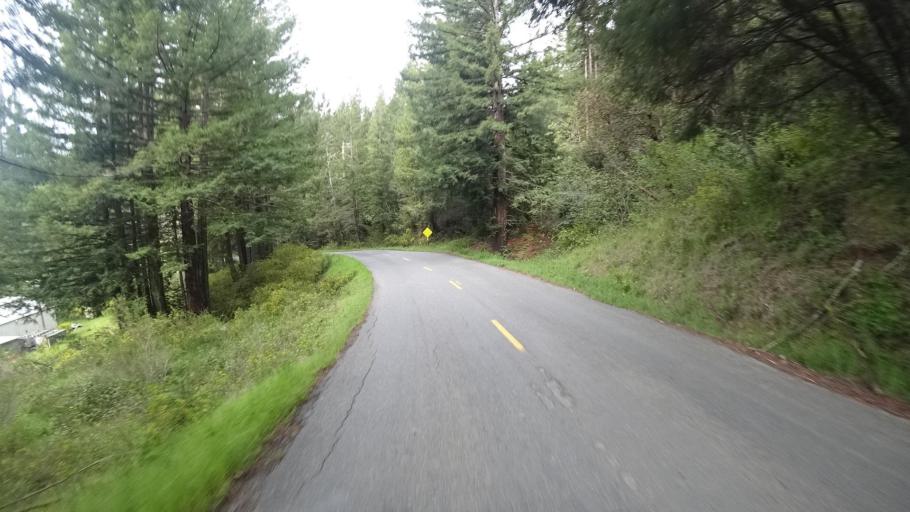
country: US
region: California
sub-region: Humboldt County
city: Redway
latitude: 40.2940
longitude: -123.8357
